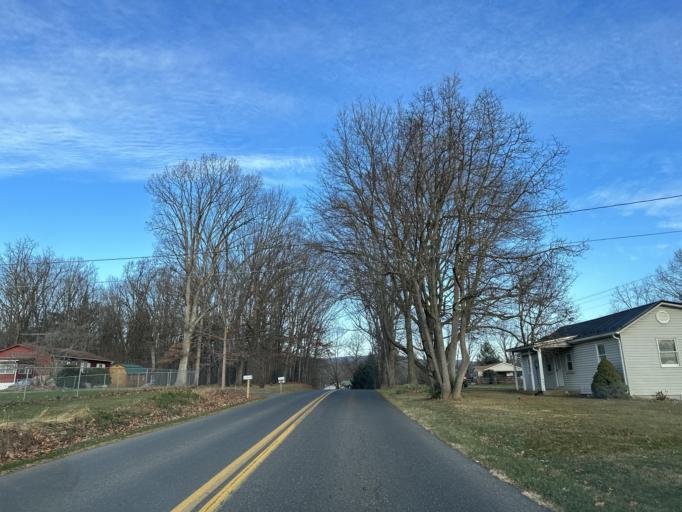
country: US
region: Virginia
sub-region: City of Staunton
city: Staunton
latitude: 38.2099
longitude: -79.2024
